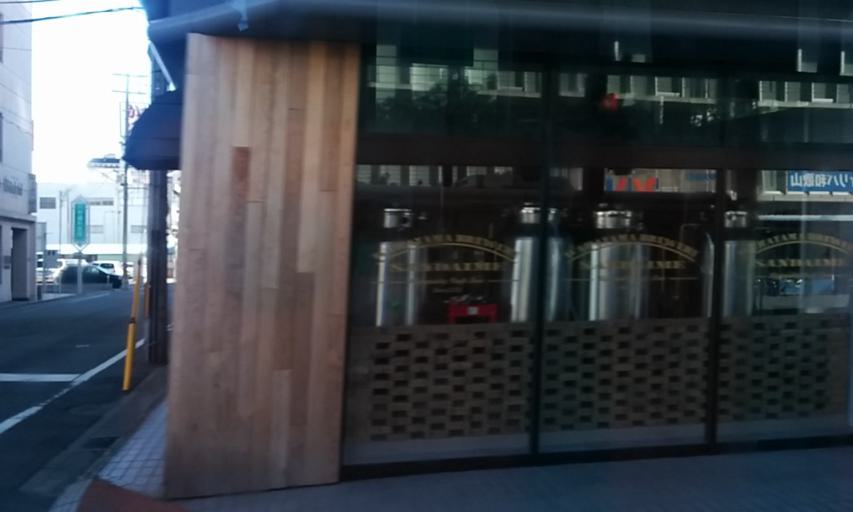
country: JP
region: Wakayama
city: Wakayama-shi
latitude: 34.2320
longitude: 135.1746
